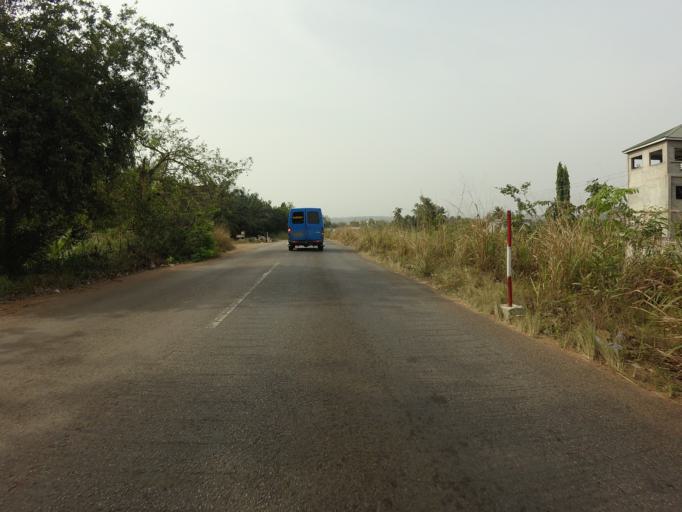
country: GH
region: Volta
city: Ho
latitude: 6.6046
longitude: 0.4526
